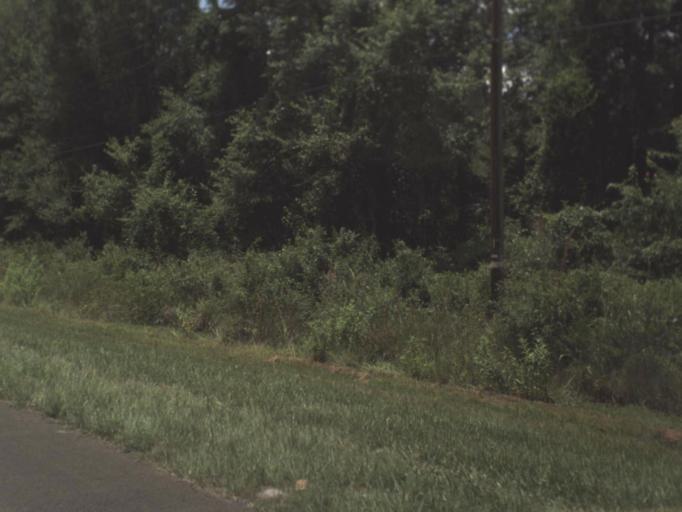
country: US
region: Florida
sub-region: Alachua County
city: Alachua
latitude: 29.7275
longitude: -82.3540
